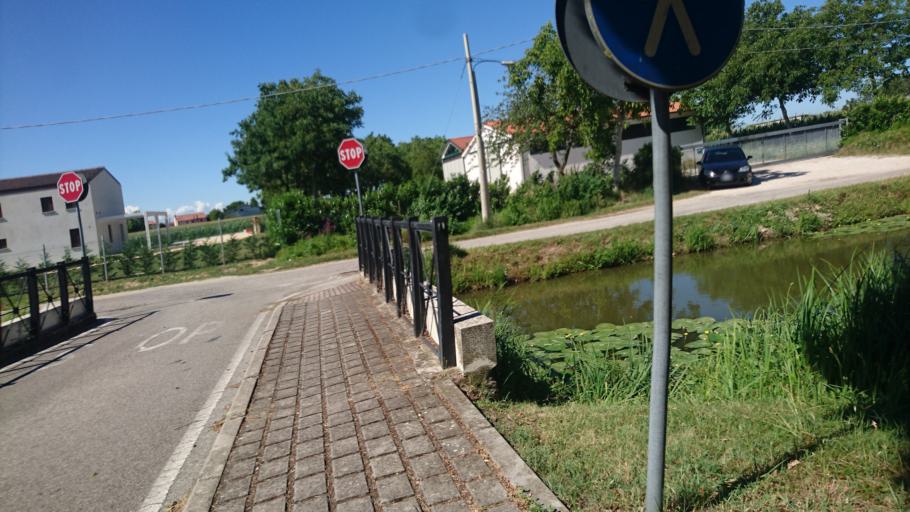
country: IT
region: Veneto
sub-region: Provincia di Padova
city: Piove di Sacco-Piovega
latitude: 45.2964
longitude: 12.0234
